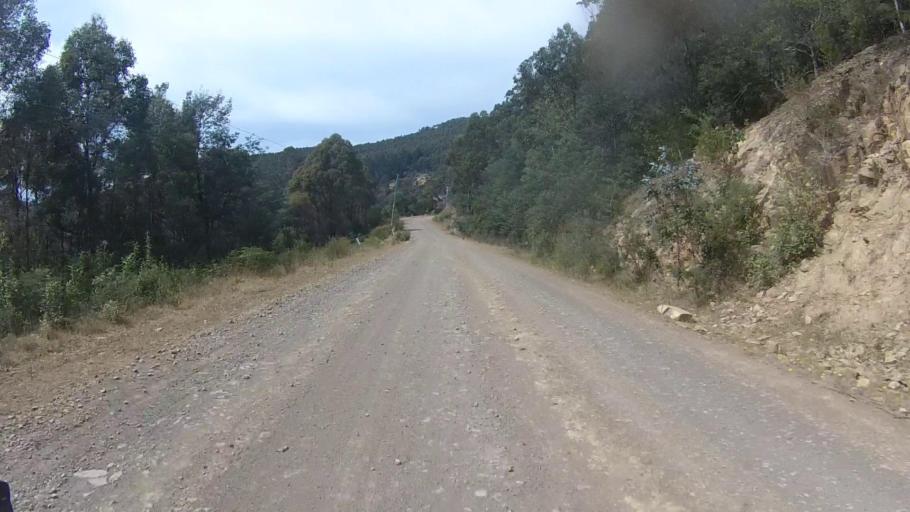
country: AU
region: Tasmania
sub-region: Sorell
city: Sorell
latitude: -42.7720
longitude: 147.8301
